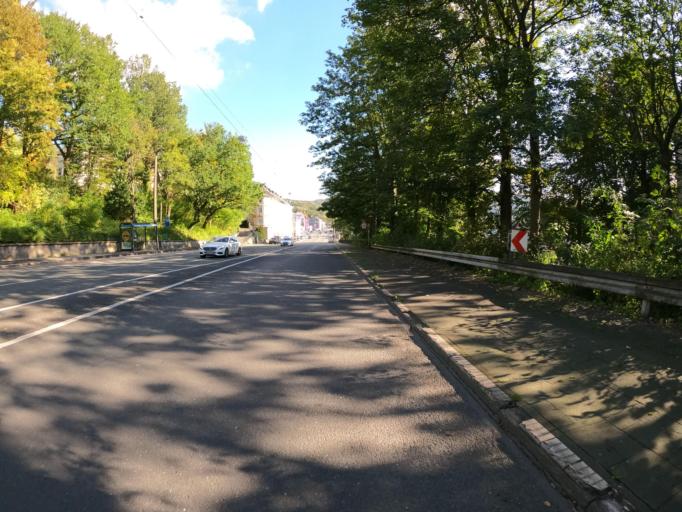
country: DE
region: North Rhine-Westphalia
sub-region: Regierungsbezirk Dusseldorf
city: Wuppertal
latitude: 51.2728
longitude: 7.2285
